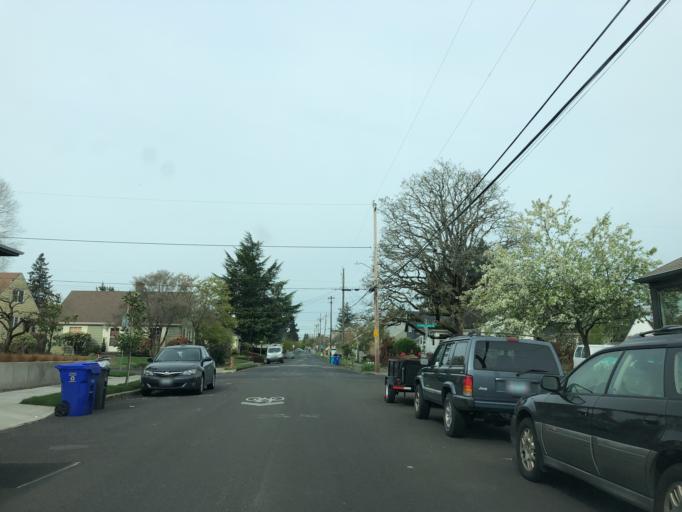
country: US
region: Oregon
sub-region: Multnomah County
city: Portland
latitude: 45.5567
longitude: -122.6230
